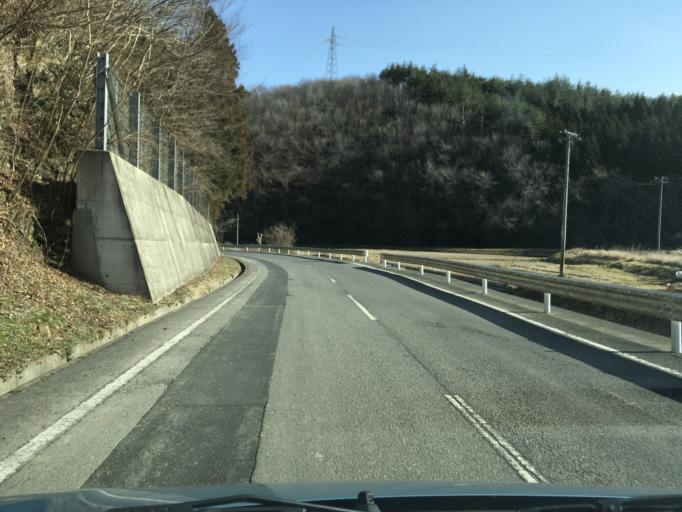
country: JP
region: Miyagi
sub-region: Oshika Gun
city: Onagawa Cho
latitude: 38.7877
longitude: 141.4541
